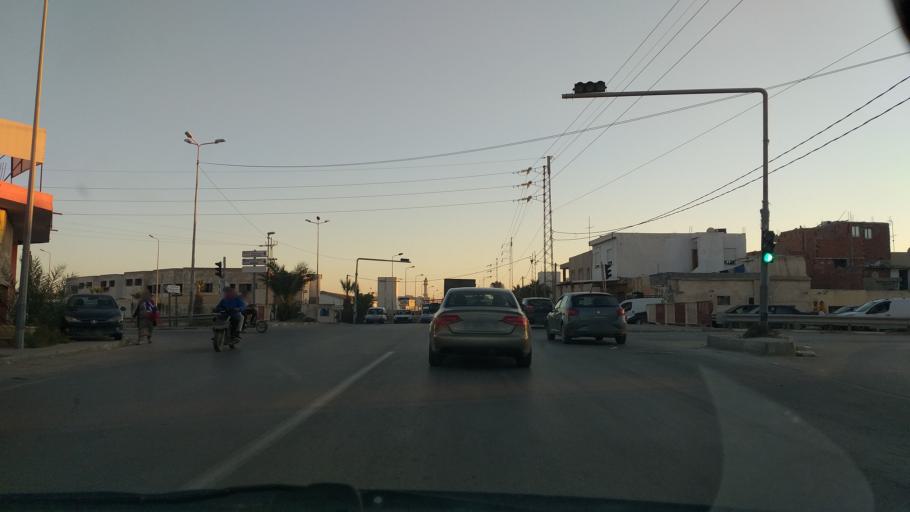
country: TN
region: Safaqis
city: Al Qarmadah
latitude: 34.7689
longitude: 10.7744
